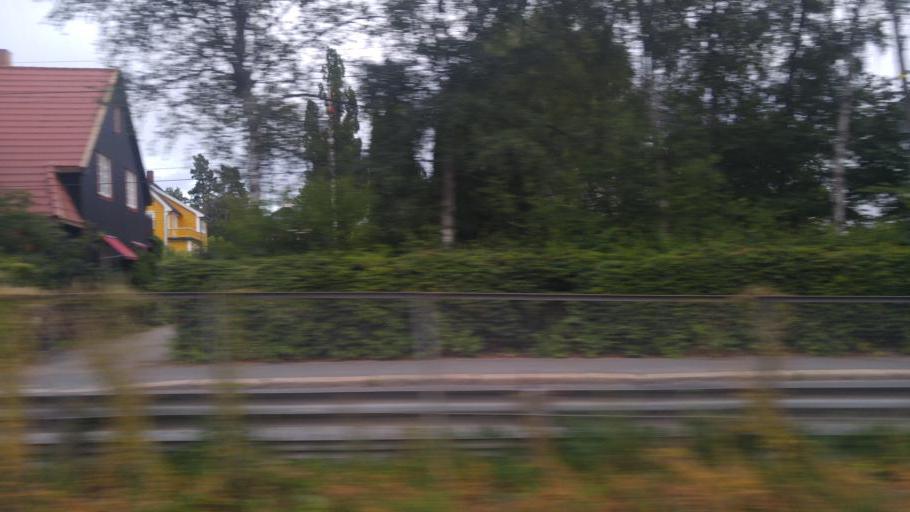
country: NO
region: Oslo
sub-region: Oslo
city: Sjolyststranda
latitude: 59.9438
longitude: 10.7063
